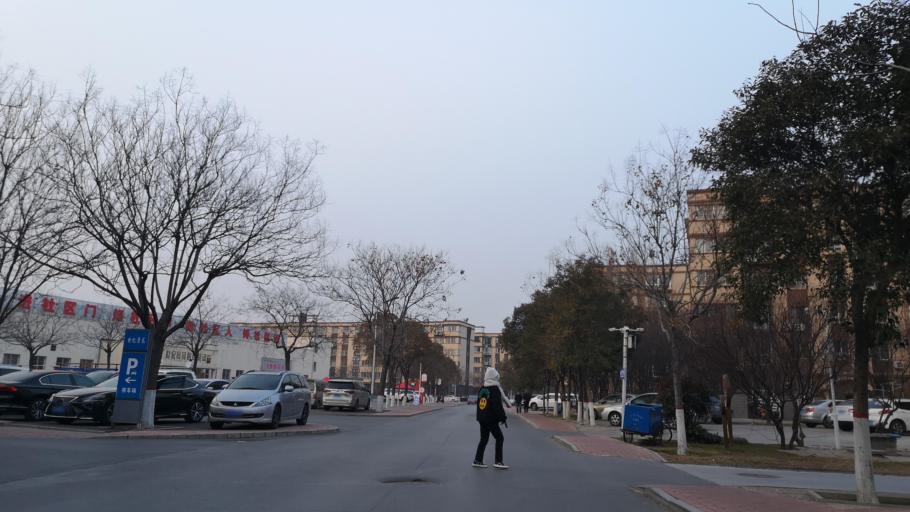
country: CN
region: Henan Sheng
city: Zhongyuanlu
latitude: 35.7861
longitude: 115.0784
